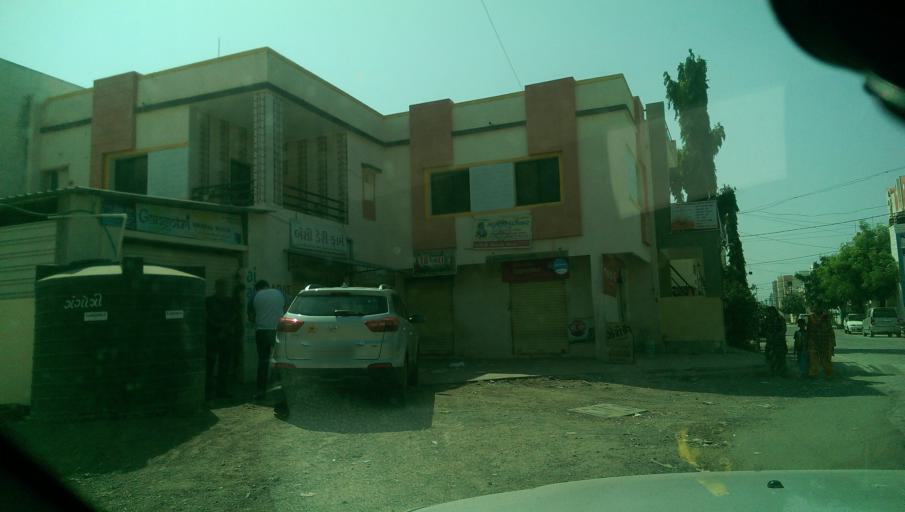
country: IN
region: Gujarat
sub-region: Jamnagar
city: Jamnagar
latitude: 22.4353
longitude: 70.0643
